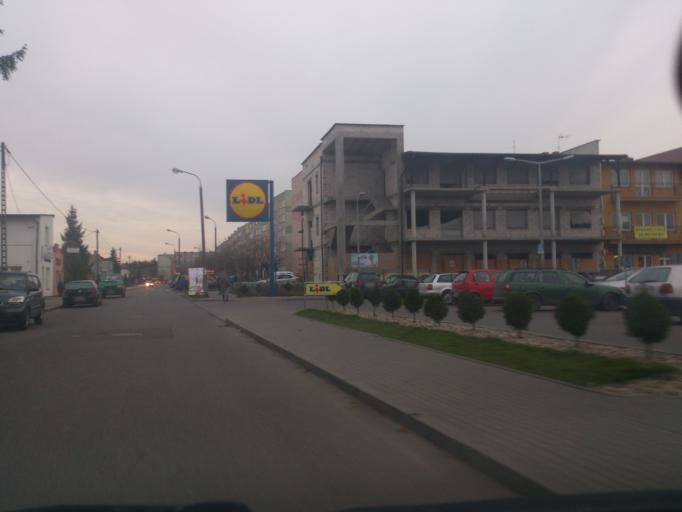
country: PL
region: Kujawsko-Pomorskie
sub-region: Powiat golubsko-dobrzynski
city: Golub-Dobrzyn
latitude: 53.1057
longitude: 19.0566
